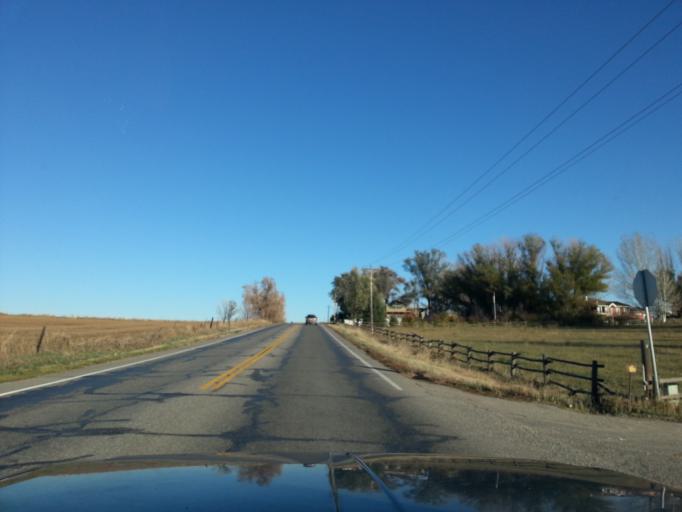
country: US
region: Colorado
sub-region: Larimer County
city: Loveland
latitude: 40.3783
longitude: -105.0191
